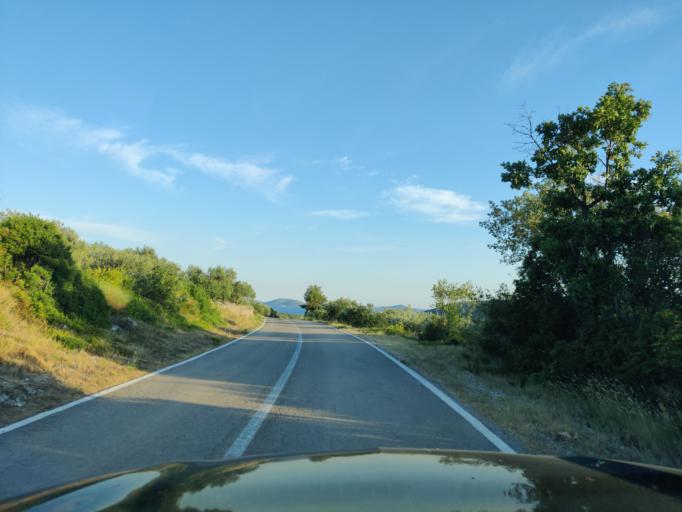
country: HR
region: Sibensko-Kniniska
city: Tribunj
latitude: 43.7845
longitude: 15.7271
